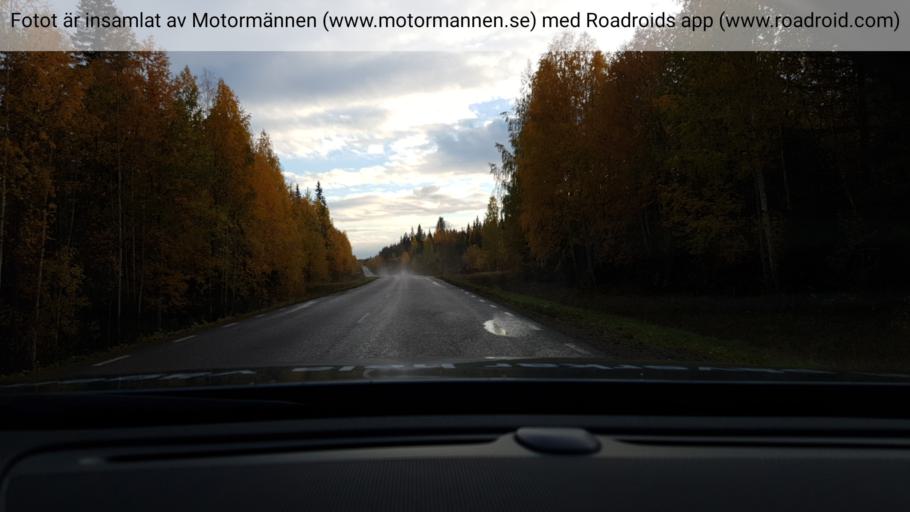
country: SE
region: Norrbotten
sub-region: Overkalix Kommun
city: OEverkalix
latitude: 66.8062
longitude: 22.7351
